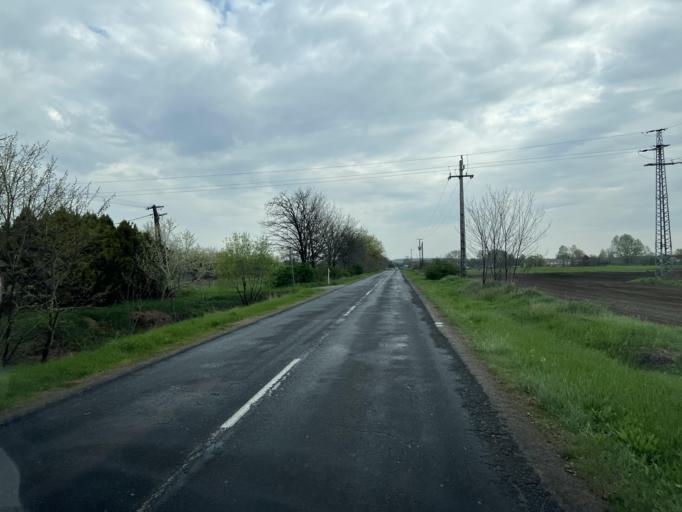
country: HU
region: Pest
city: Albertirsa
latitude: 47.2389
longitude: 19.5929
